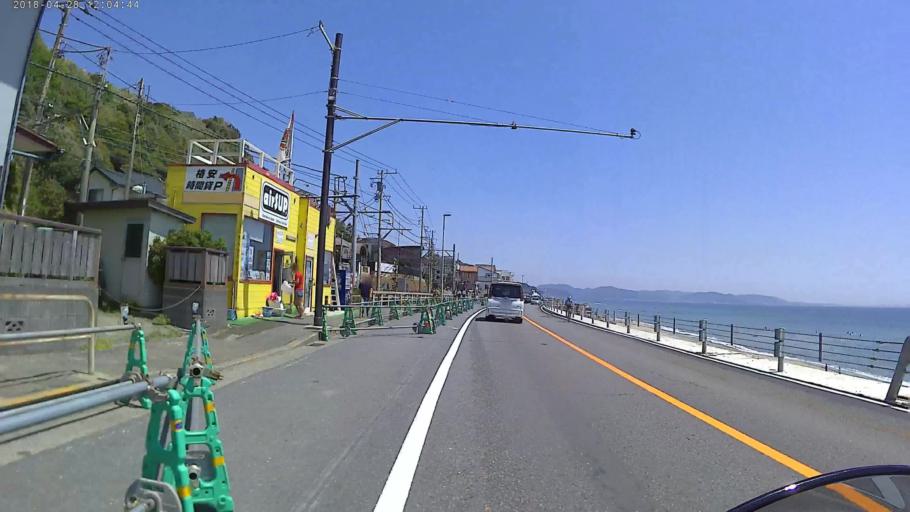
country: JP
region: Kanagawa
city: Kamakura
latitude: 35.3062
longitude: 139.5054
